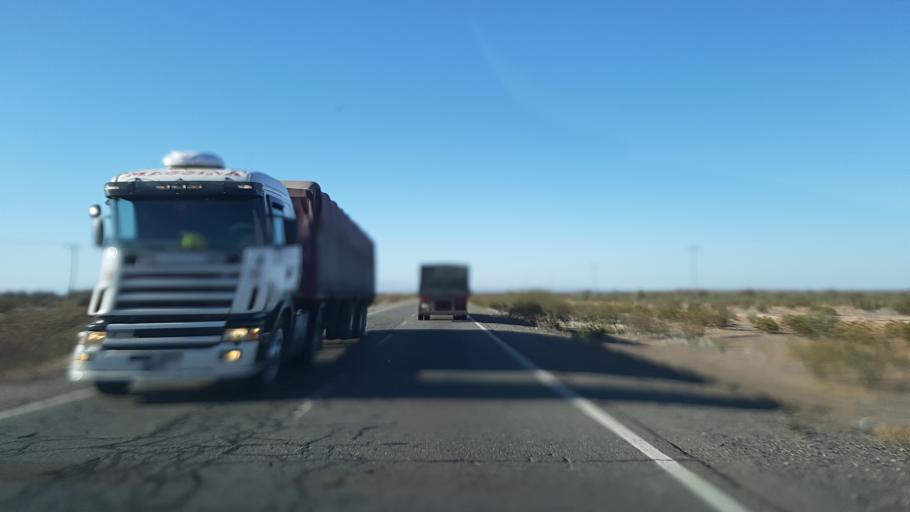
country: AR
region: San Juan
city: Caucete
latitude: -31.6526
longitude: -67.7673
